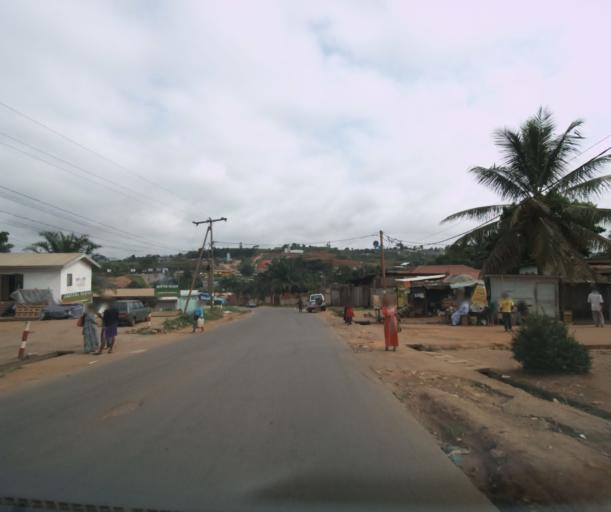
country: CM
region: Centre
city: Yaounde
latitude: 3.8050
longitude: 11.5215
